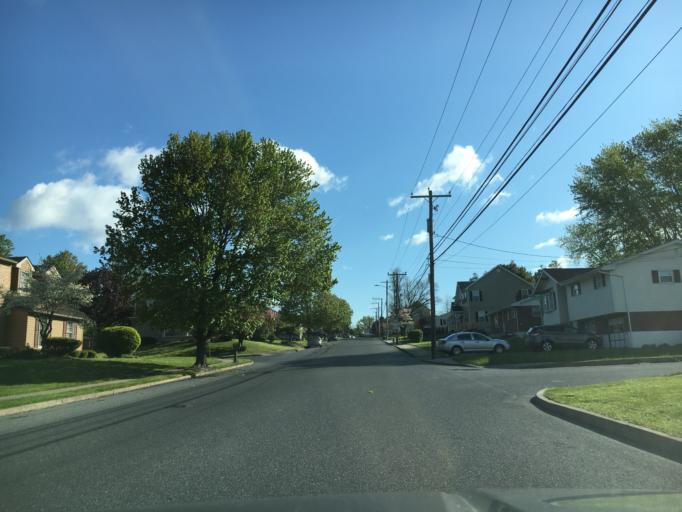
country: US
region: Pennsylvania
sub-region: Lehigh County
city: Stiles
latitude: 40.6680
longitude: -75.5096
